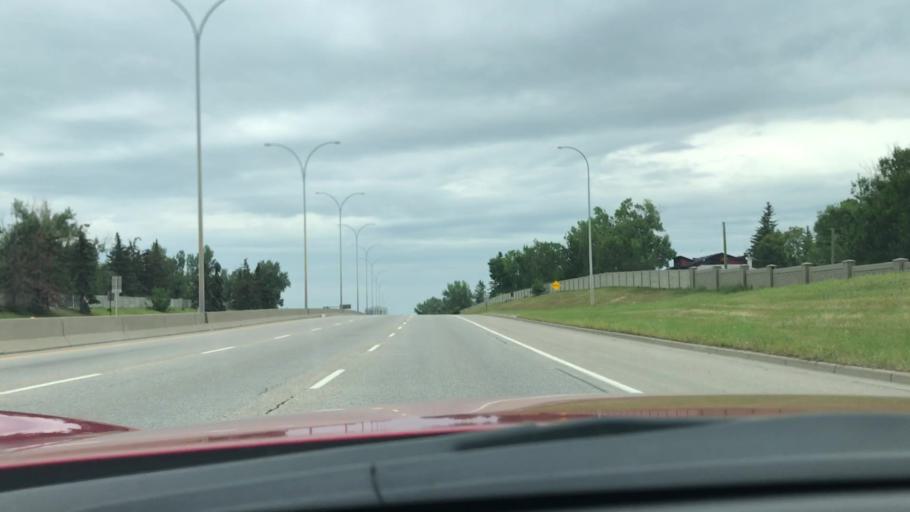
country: CA
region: Alberta
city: Calgary
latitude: 51.0247
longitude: -114.1177
